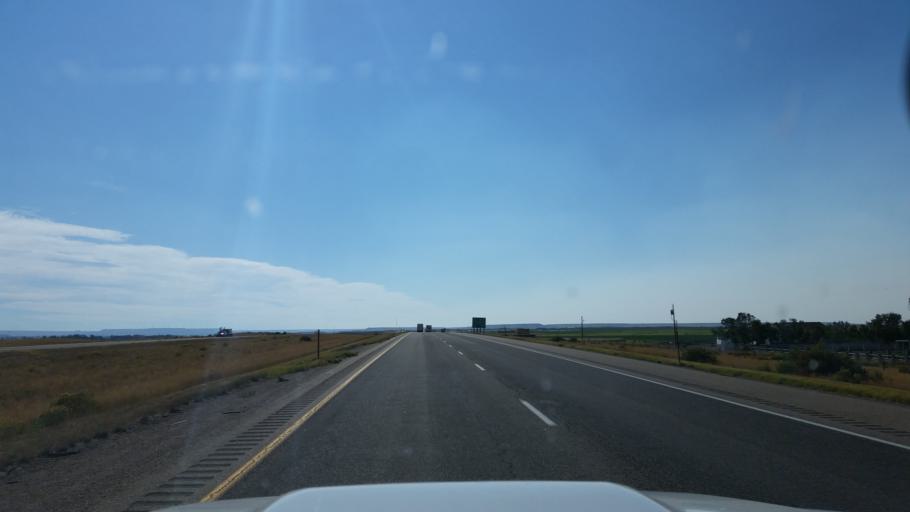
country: US
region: Wyoming
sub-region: Uinta County
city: Lyman
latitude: 41.3712
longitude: -110.2677
